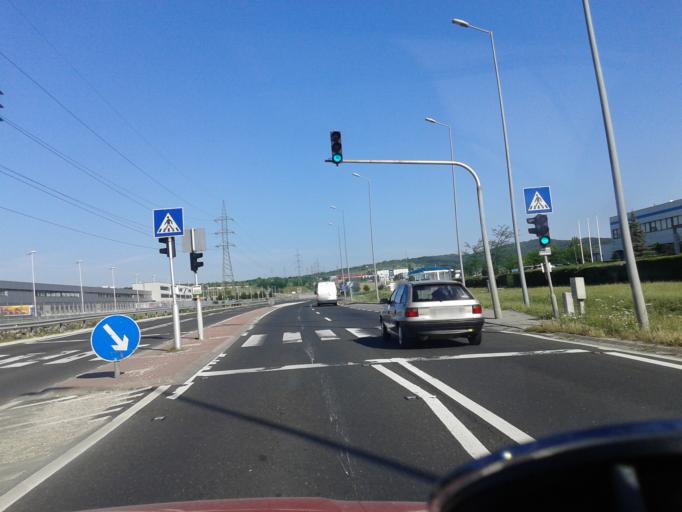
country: HU
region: Pest
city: Toeroekbalint
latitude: 47.4679
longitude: 18.8753
